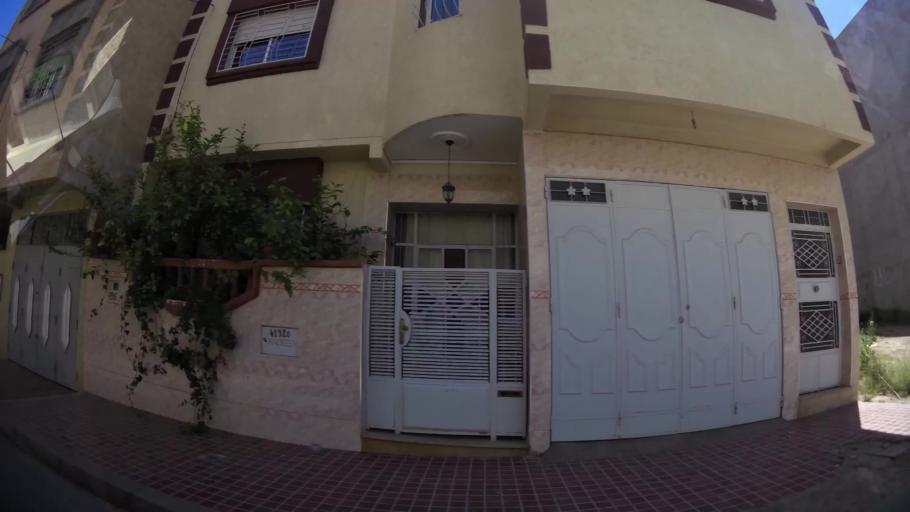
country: MA
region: Oriental
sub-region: Oujda-Angad
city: Oujda
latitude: 34.6569
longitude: -1.8838
